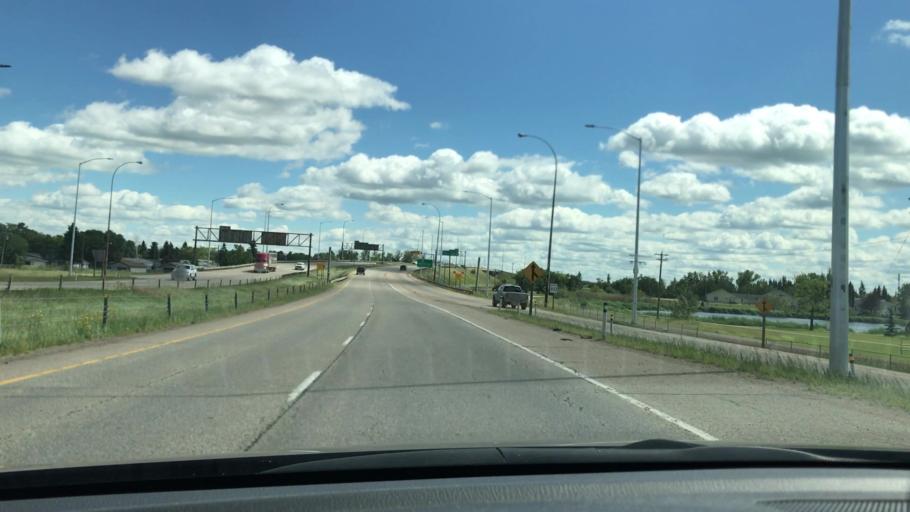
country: CA
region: Alberta
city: Leduc
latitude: 53.2626
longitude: -113.5635
